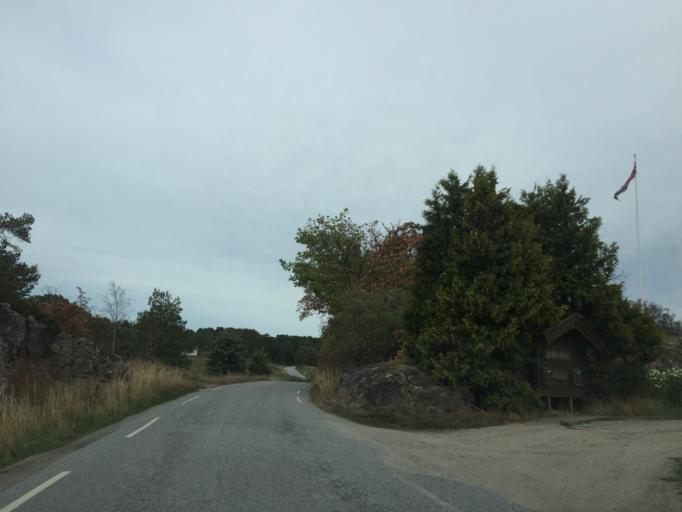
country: NO
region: Ostfold
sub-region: Hvaler
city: Skjaerhalden
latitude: 59.0448
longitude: 11.0339
